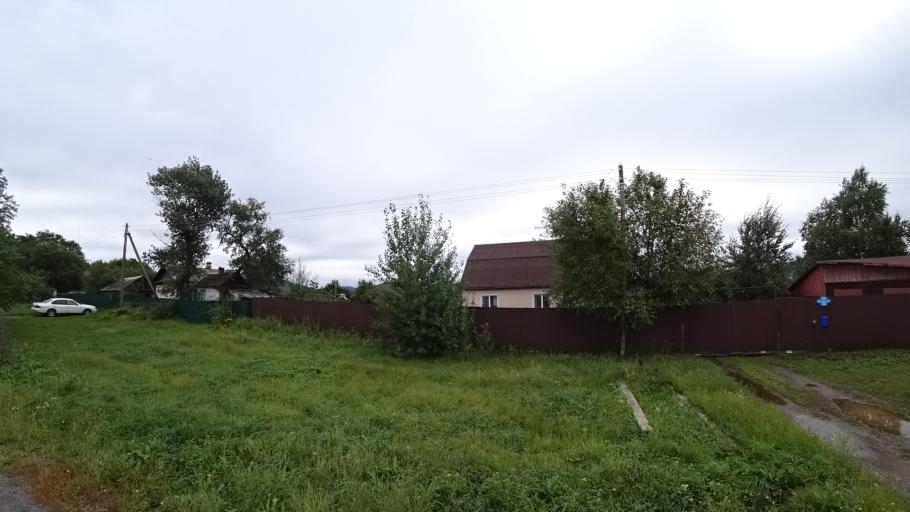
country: RU
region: Primorskiy
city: Monastyrishche
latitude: 44.1904
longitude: 132.4913
